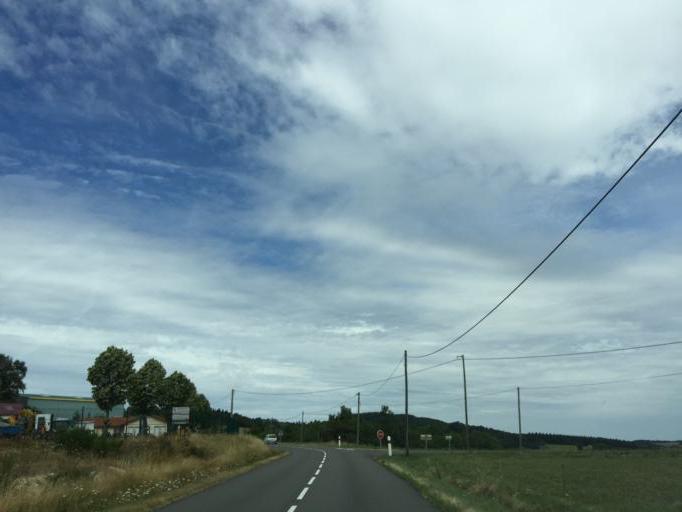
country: FR
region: Rhone-Alpes
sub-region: Departement de la Loire
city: Saint-Bonnet-le-Chateau
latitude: 45.4127
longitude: 4.0939
